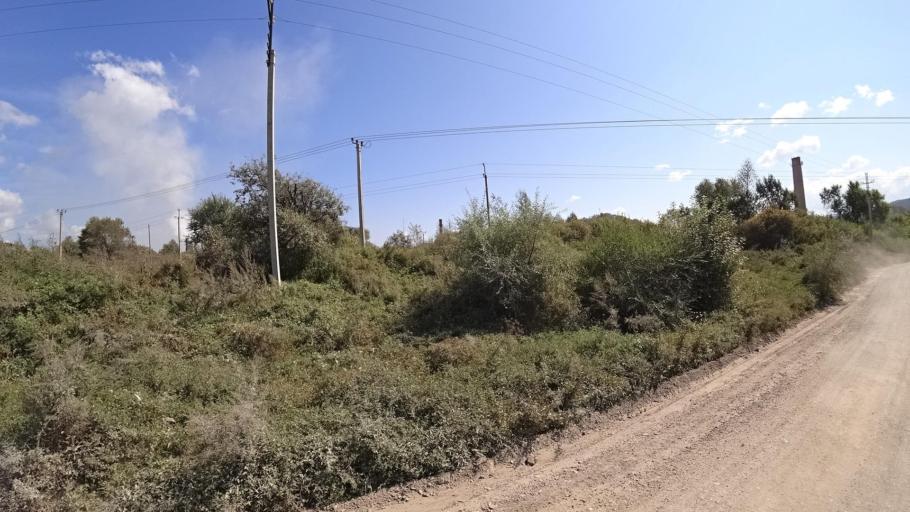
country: RU
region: Jewish Autonomous Oblast
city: Londoko
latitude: 49.0060
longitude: 131.8899
